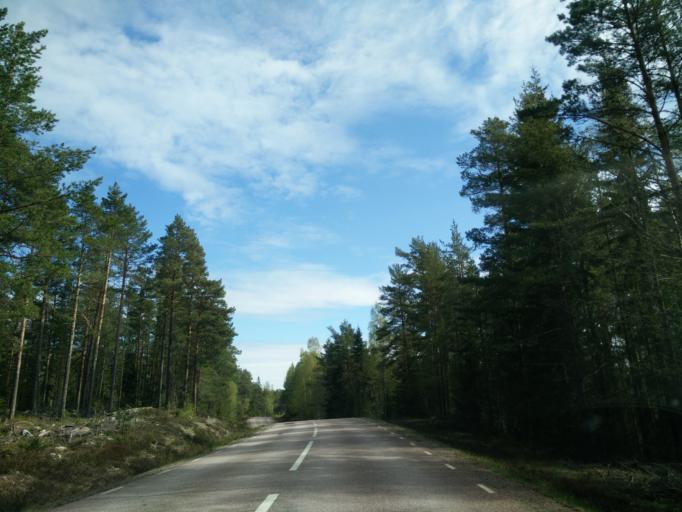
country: SE
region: Gaevleborg
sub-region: Hudiksvalls Kommun
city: Hudiksvall
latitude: 61.8464
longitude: 17.2708
